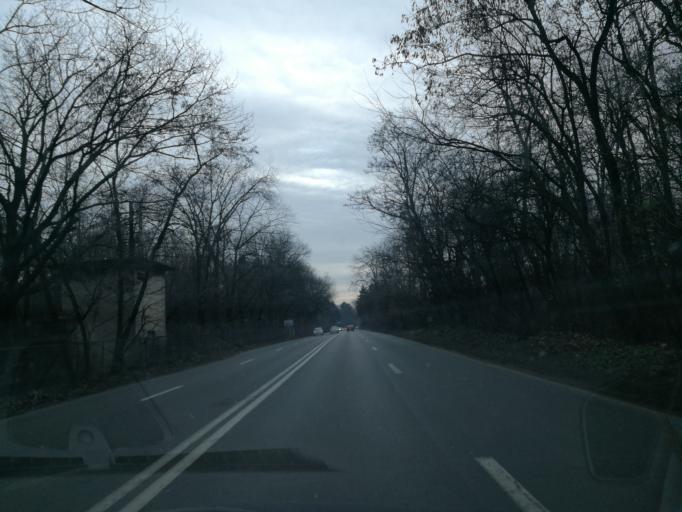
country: RO
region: Ilfov
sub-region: Voluntari City
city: Voluntari
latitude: 44.5050
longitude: 26.1834
